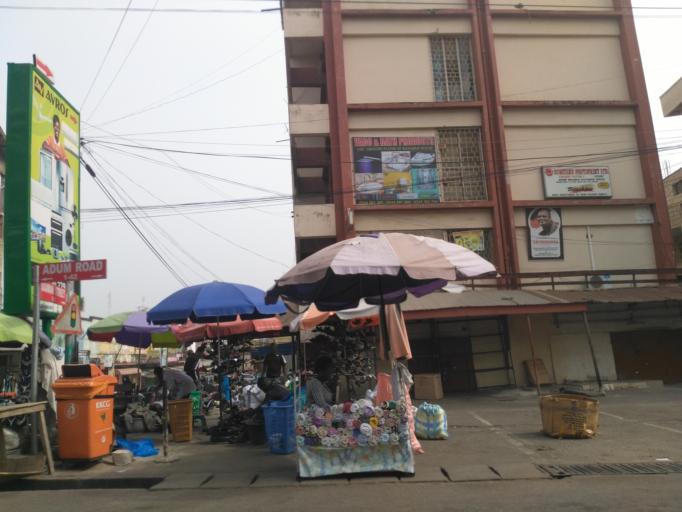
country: GH
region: Ashanti
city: Kumasi
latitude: 6.6916
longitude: -1.6216
